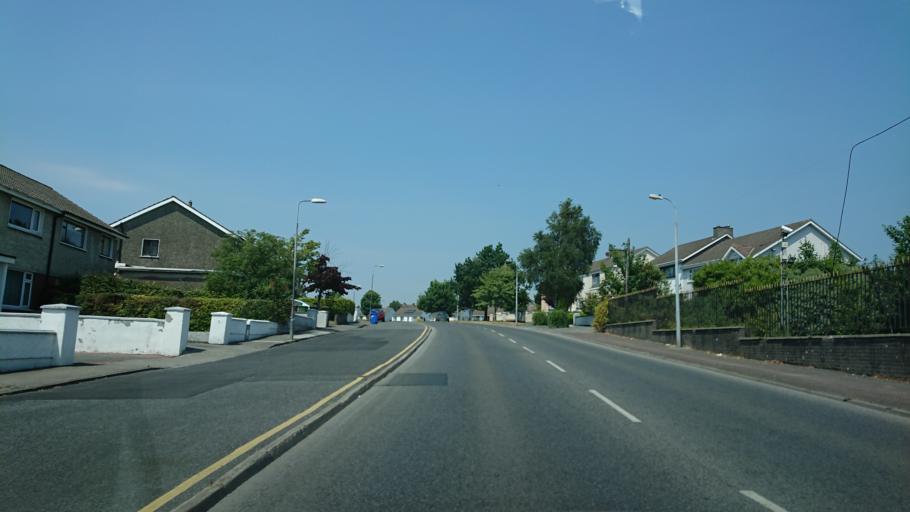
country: IE
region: Munster
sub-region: Waterford
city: Waterford
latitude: 52.2460
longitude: -7.1344
